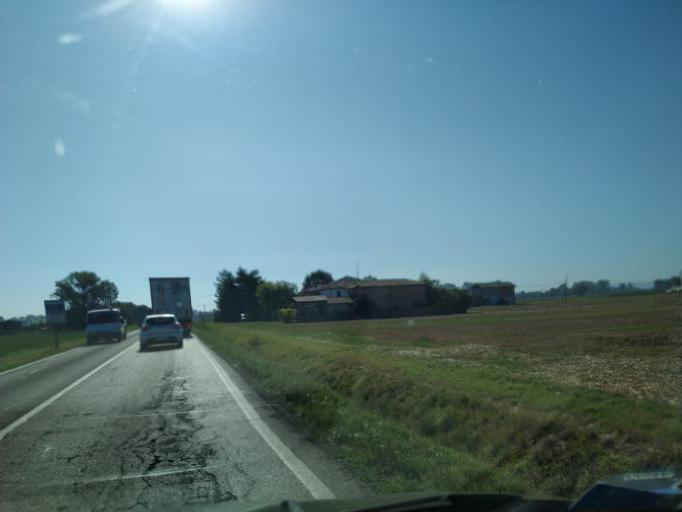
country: IT
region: Emilia-Romagna
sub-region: Provincia di Bologna
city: Sant'Agata Bolognese
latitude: 44.6686
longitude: 11.0976
